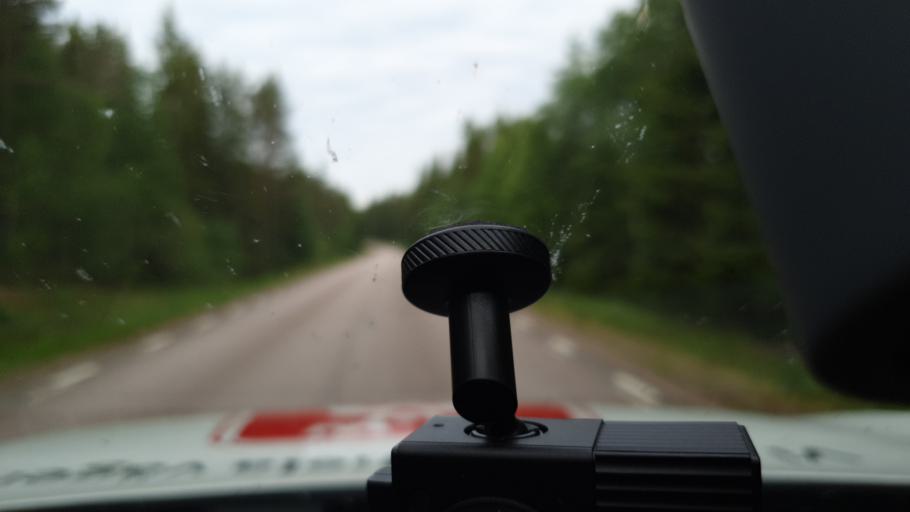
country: SE
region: Vaermland
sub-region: Torsby Kommun
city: Torsby
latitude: 60.1118
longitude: 12.9193
